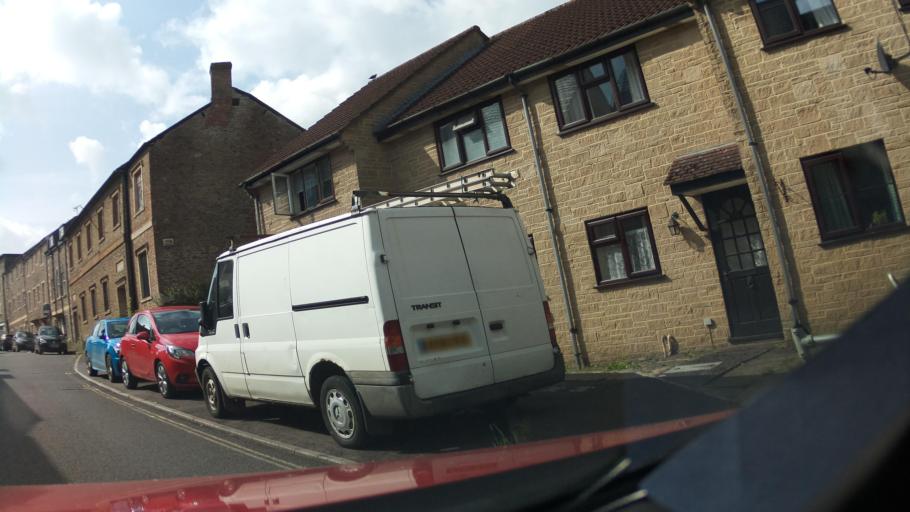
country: GB
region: England
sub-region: Somerset
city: Wincanton
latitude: 51.0569
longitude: -2.4119
